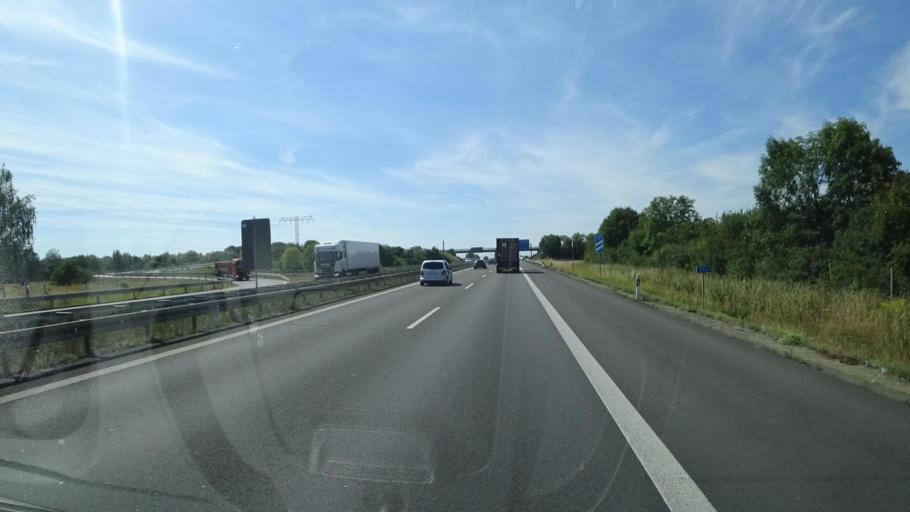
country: DE
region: Brandenburg
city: Frankfurt (Oder)
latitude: 52.3207
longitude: 14.4790
